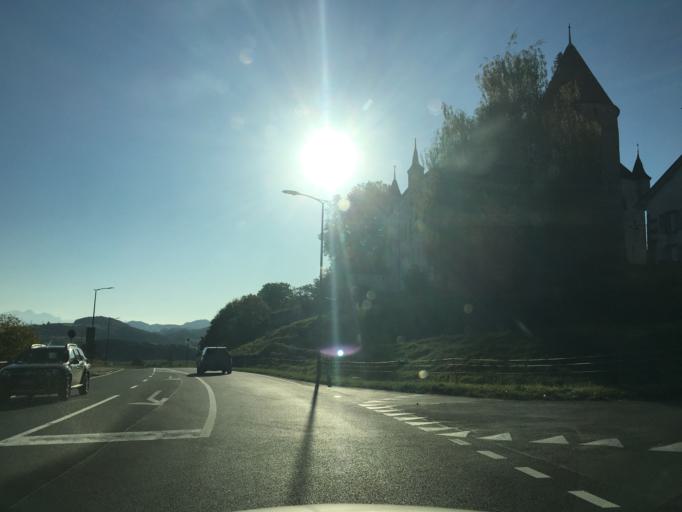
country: CH
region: Vaud
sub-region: Lavaux-Oron District
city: Oron-la-ville
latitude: 46.5750
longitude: 6.8386
